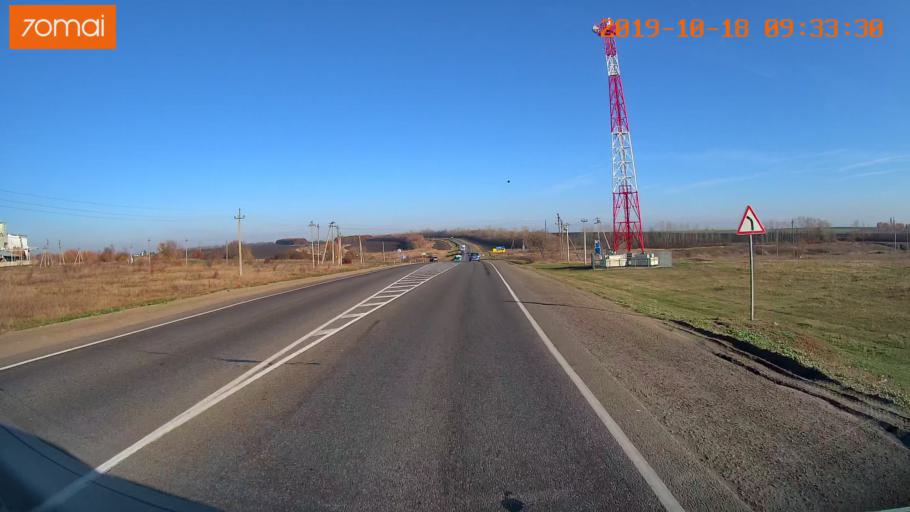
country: RU
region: Tula
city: Yefremov
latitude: 53.1676
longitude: 38.1511
